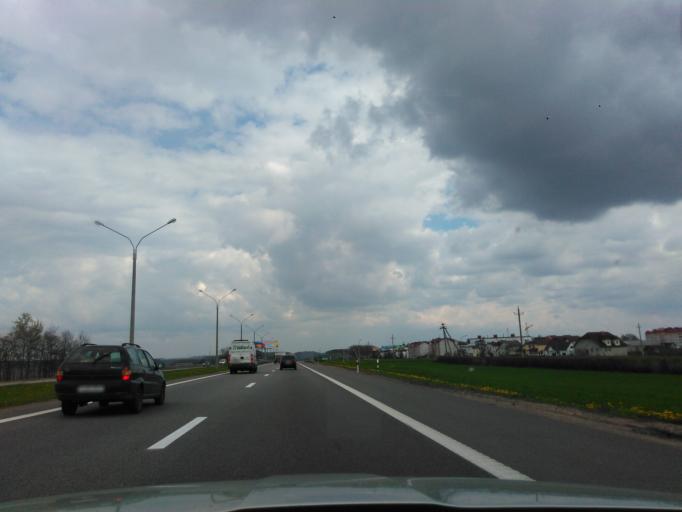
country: BY
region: Minsk
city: Slabada
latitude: 54.0099
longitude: 27.8607
